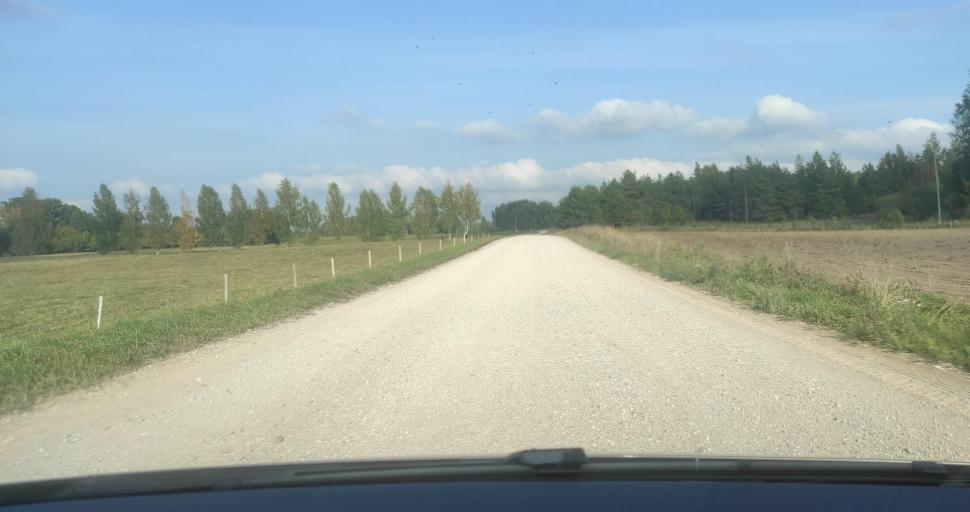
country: LV
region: Alsunga
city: Alsunga
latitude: 56.9999
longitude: 21.5898
